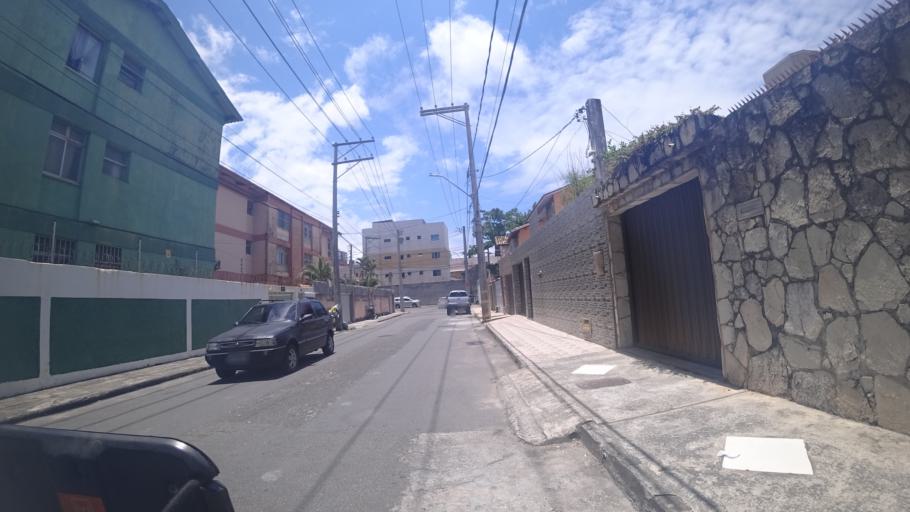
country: BR
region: Bahia
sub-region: Salvador
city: Salvador
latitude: -13.0108
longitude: -38.4687
